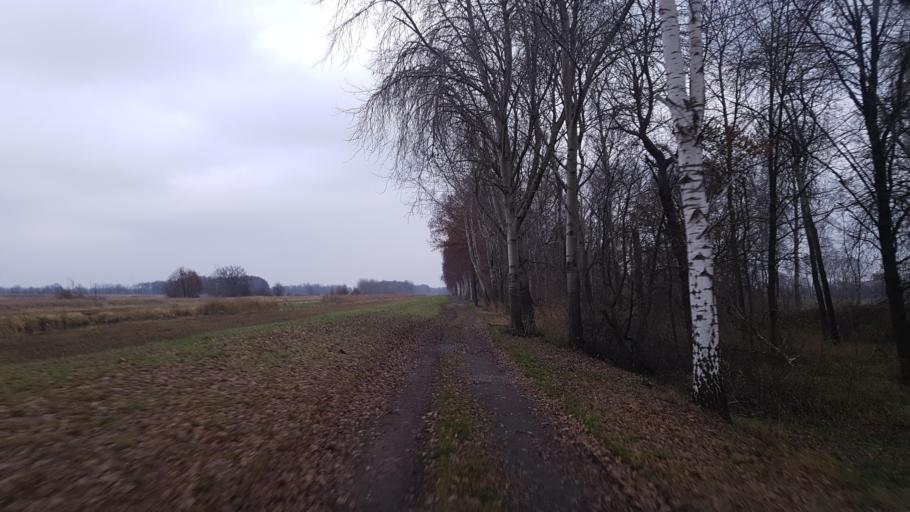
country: DE
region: Brandenburg
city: Schraden
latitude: 51.4602
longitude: 13.6923
